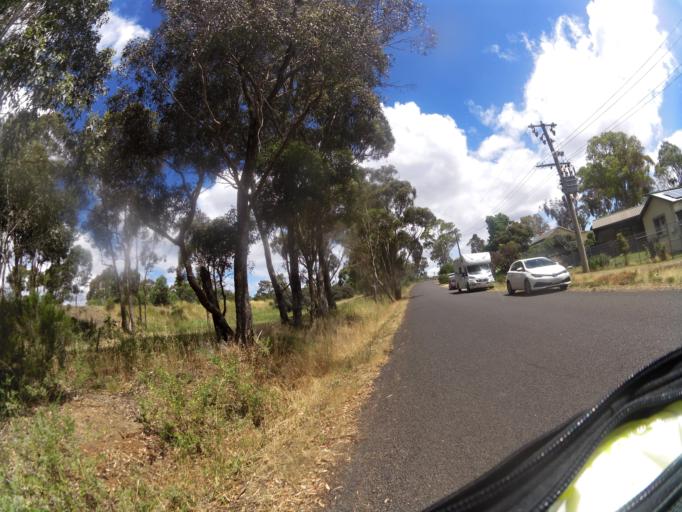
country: AU
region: Victoria
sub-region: Mount Alexander
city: Castlemaine
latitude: -37.0020
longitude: 144.2539
